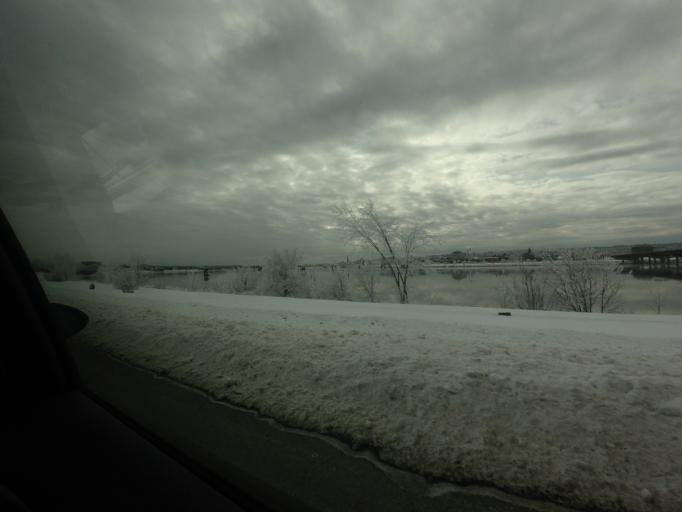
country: CA
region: New Brunswick
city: Fredericton
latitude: 45.9708
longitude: -66.6394
